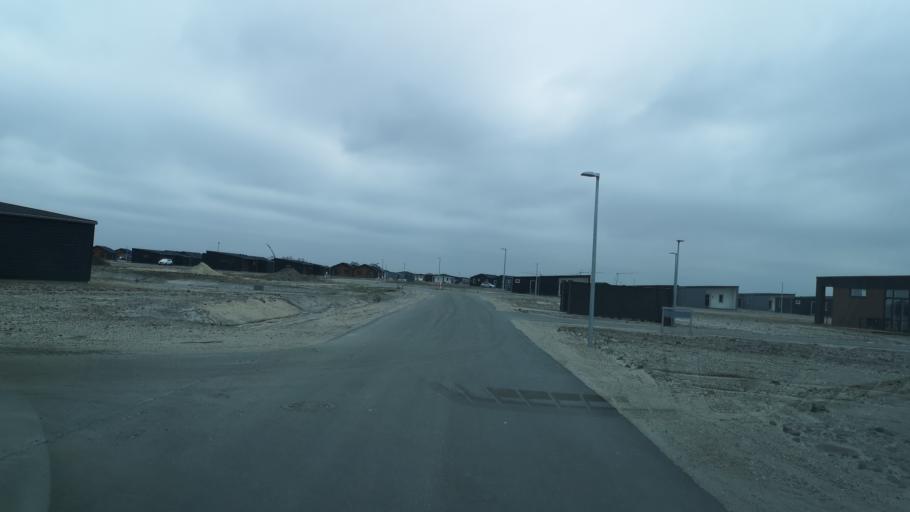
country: DK
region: Central Jutland
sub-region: Ringkobing-Skjern Kommune
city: Hvide Sande
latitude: 56.1297
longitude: 8.1220
